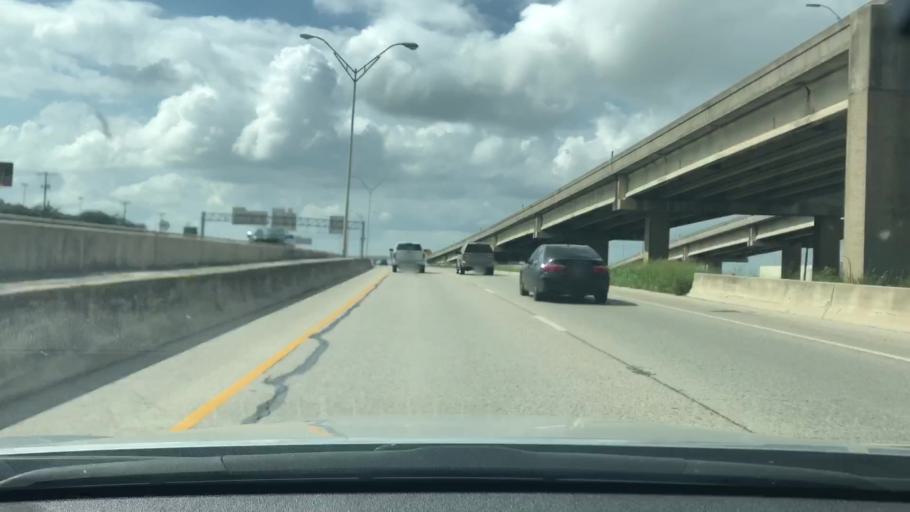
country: US
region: Texas
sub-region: Bexar County
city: Windcrest
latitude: 29.5198
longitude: -98.3980
